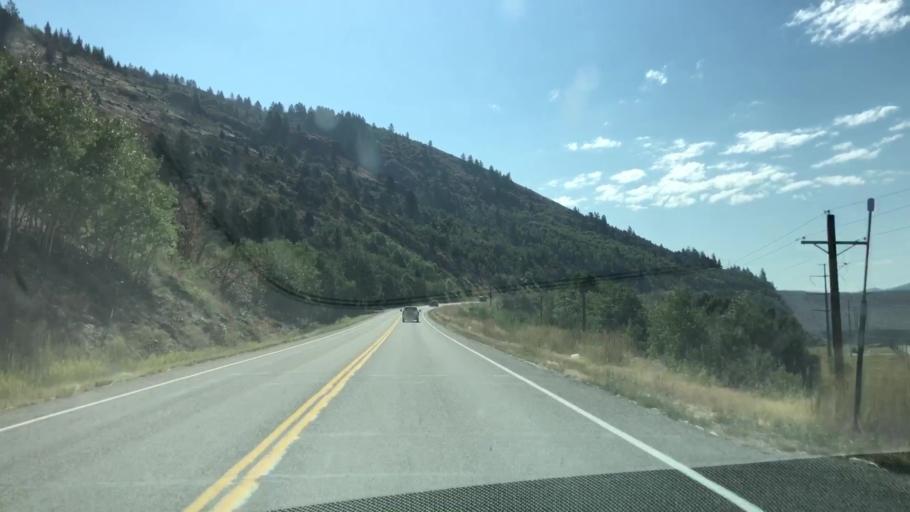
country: US
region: Idaho
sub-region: Teton County
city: Victor
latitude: 43.3443
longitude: -111.2057
